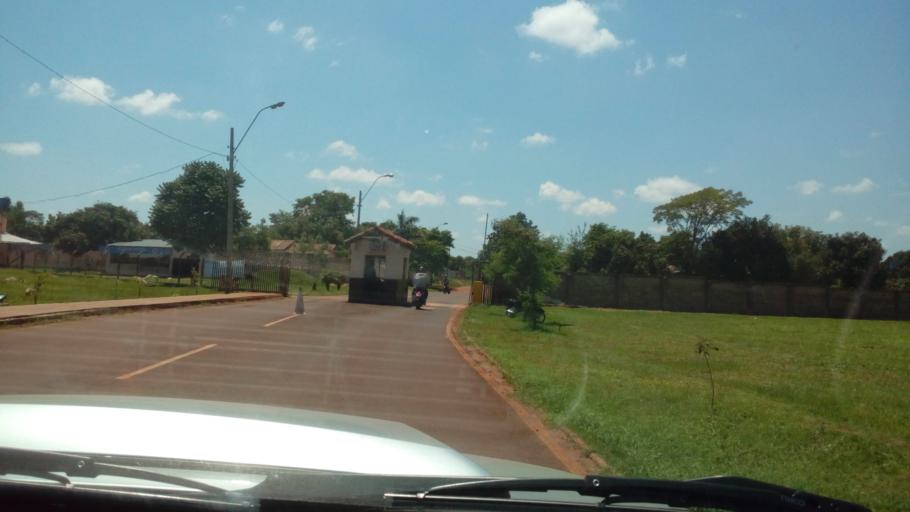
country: PY
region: Alto Parana
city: Ciudad del Este
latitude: -25.4852
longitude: -54.6672
